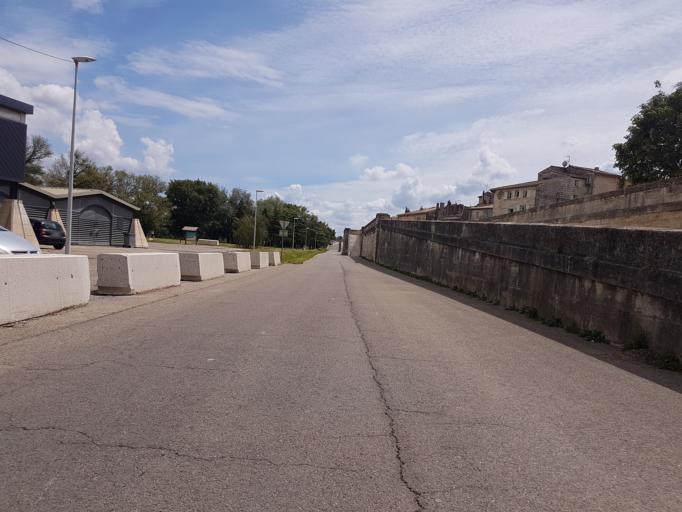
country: FR
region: Languedoc-Roussillon
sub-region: Departement du Gard
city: Beaucaire
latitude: 43.8084
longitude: 4.6477
